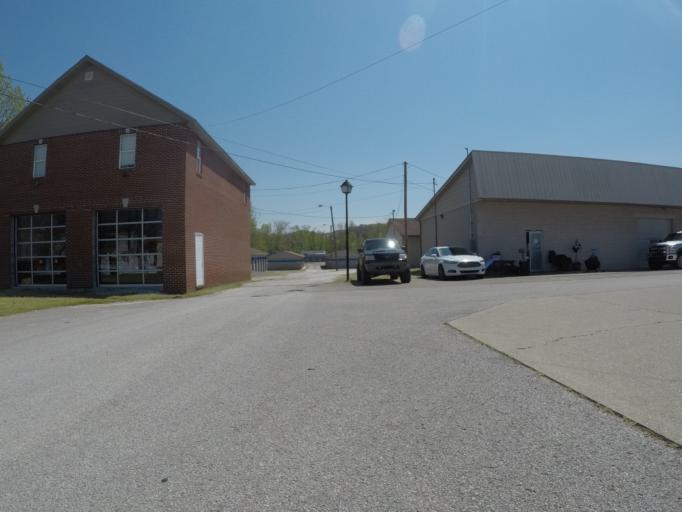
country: US
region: West Virginia
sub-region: Cabell County
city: Barboursville
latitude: 38.4120
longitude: -82.2998
